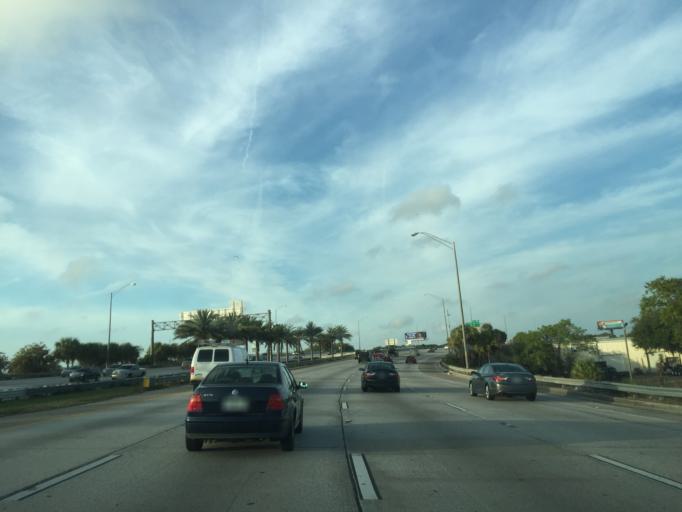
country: US
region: Florida
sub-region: Pinellas County
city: Saint Petersburg
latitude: 27.7830
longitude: -82.6612
